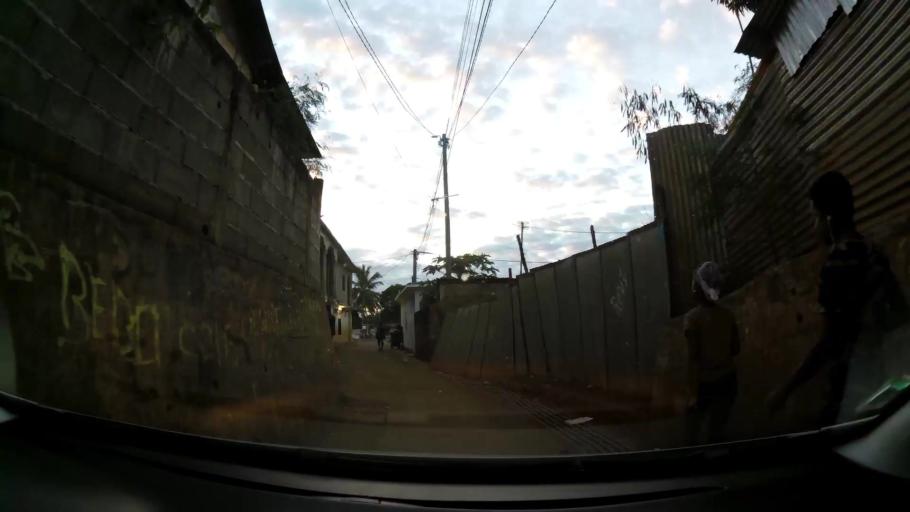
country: YT
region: Koungou
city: Koungou
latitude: -12.7337
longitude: 45.1611
